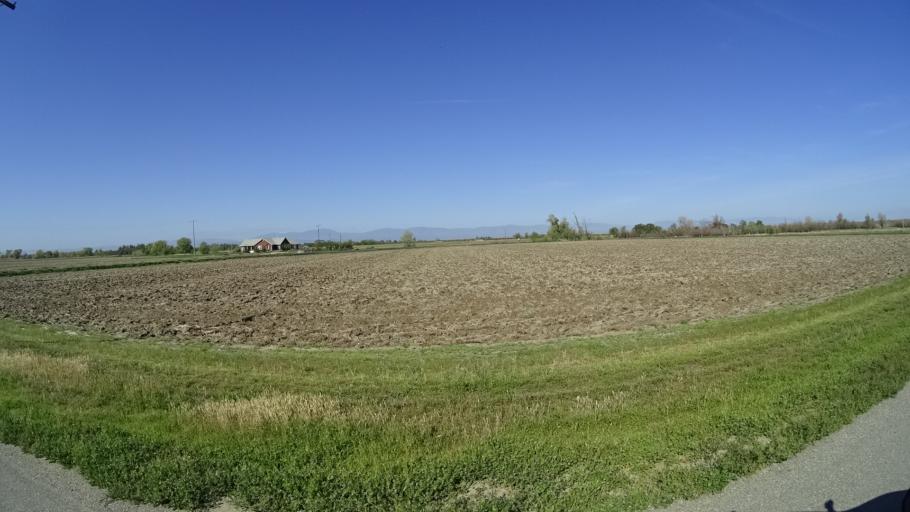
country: US
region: California
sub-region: Glenn County
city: Willows
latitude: 39.5452
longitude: -122.1696
